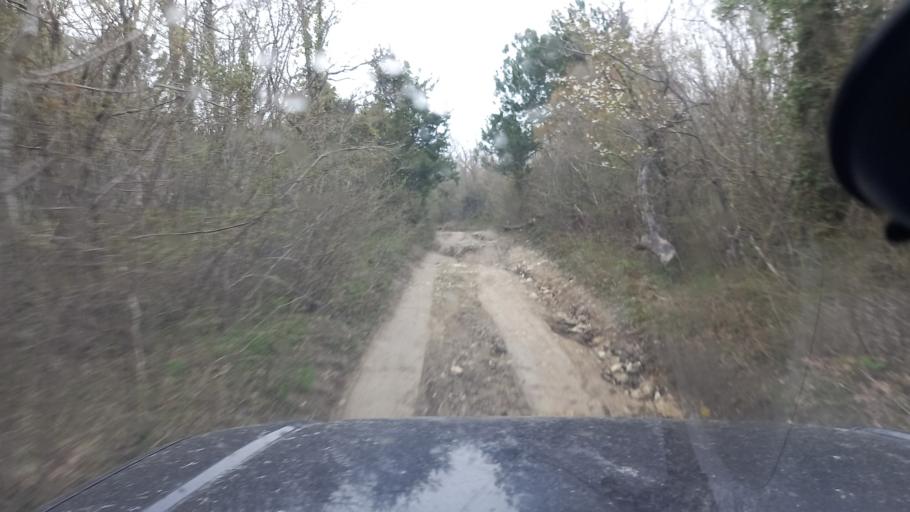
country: RU
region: Krasnodarskiy
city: Dzhubga
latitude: 44.3168
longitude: 38.6795
